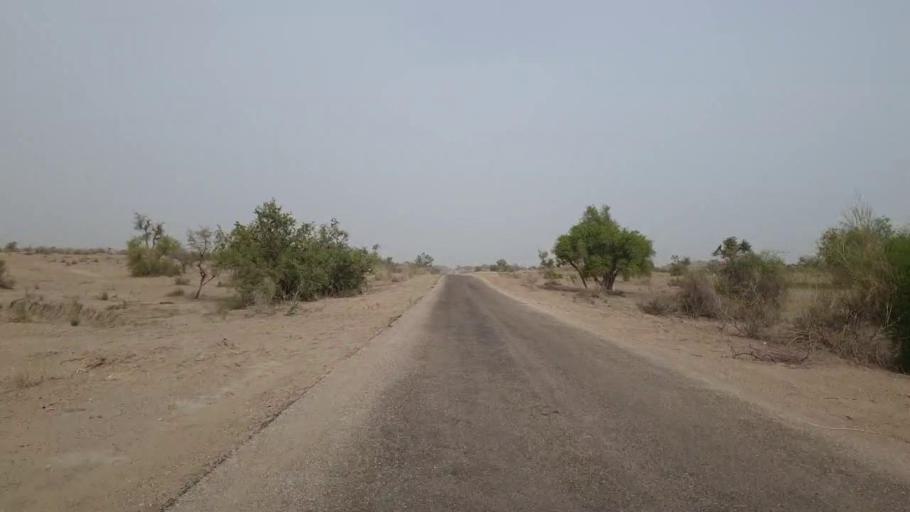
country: PK
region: Sindh
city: Islamkot
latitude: 24.5654
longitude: 70.3318
